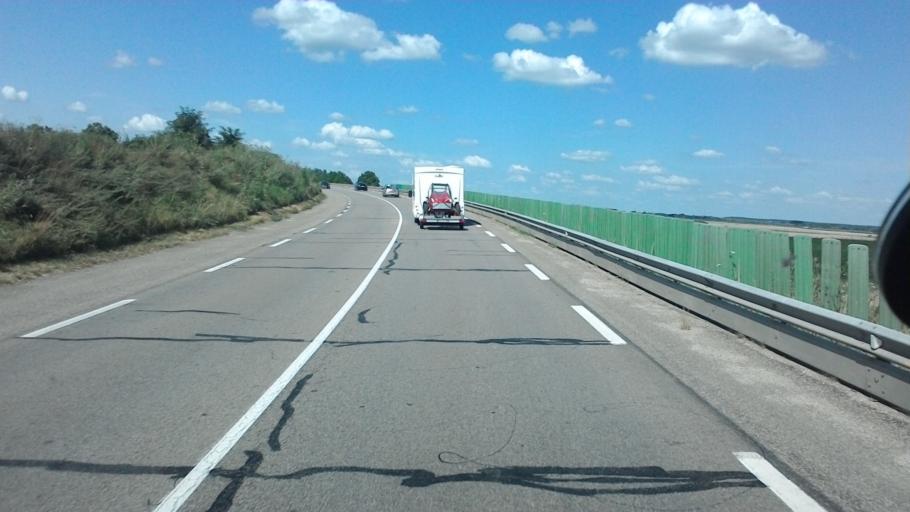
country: FR
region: Franche-Comte
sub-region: Departement du Jura
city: Tavaux
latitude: 47.0347
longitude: 5.4132
